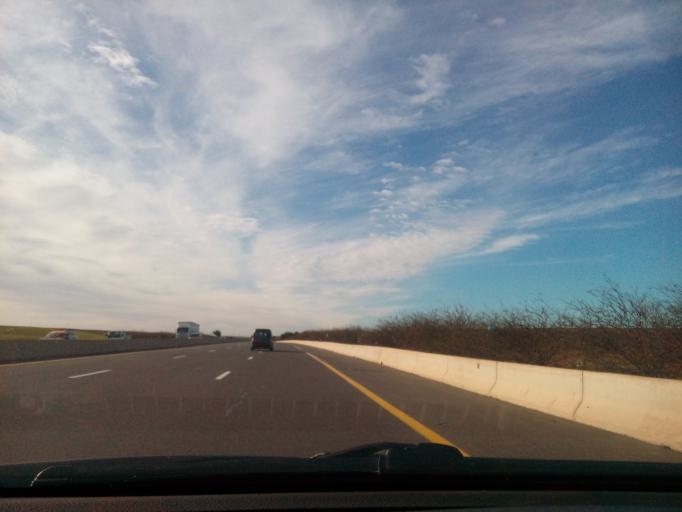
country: DZ
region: Sidi Bel Abbes
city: Sidi Bel Abbes
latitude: 35.1687
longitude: -0.7646
